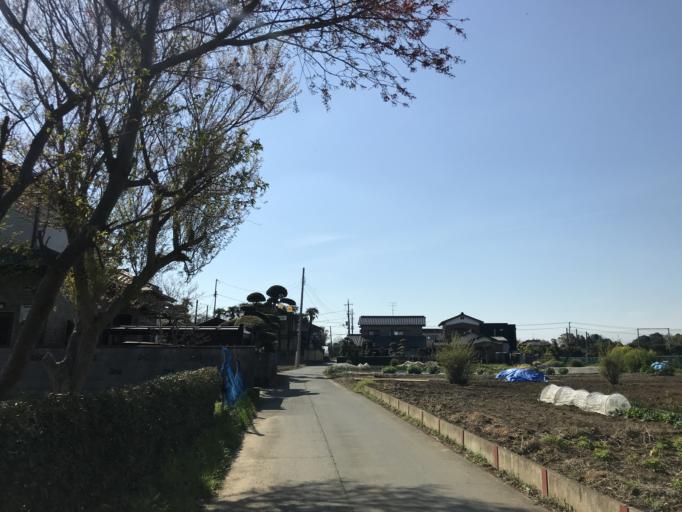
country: JP
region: Ibaraki
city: Moriya
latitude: 35.9616
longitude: 139.9565
